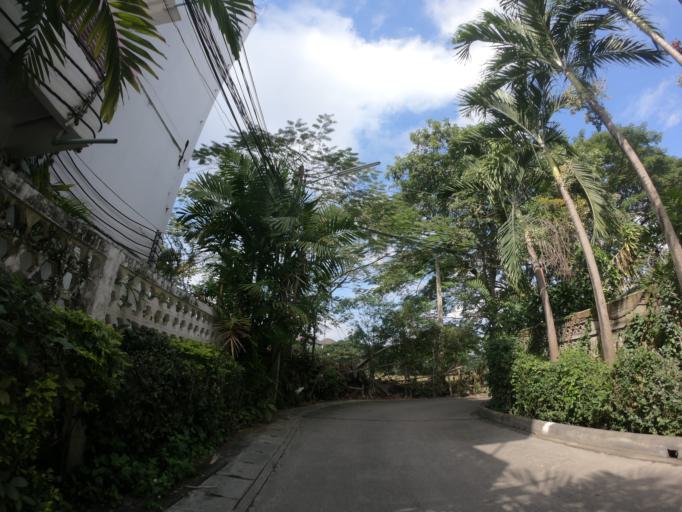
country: TH
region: Chiang Mai
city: Chiang Mai
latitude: 18.7933
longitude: 99.0270
